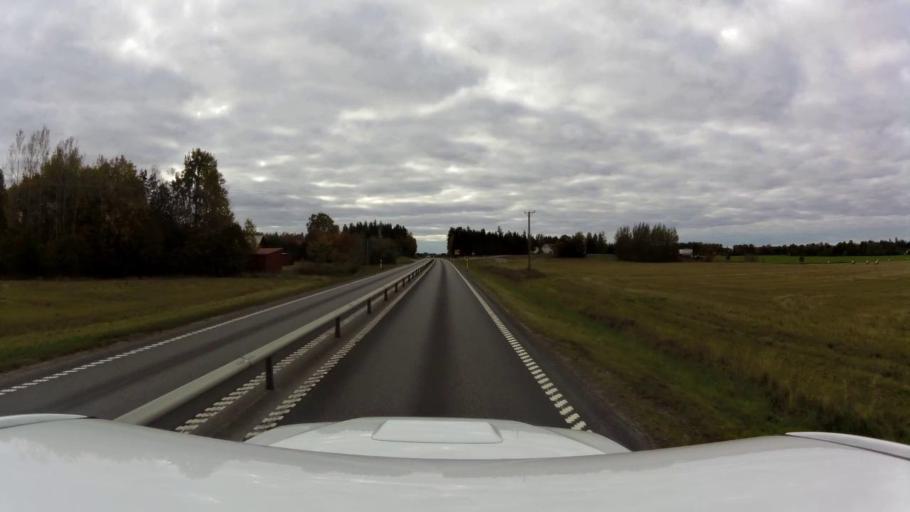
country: SE
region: OEstergoetland
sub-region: Linkopings Kommun
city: Malmslatt
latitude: 58.3599
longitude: 15.5454
